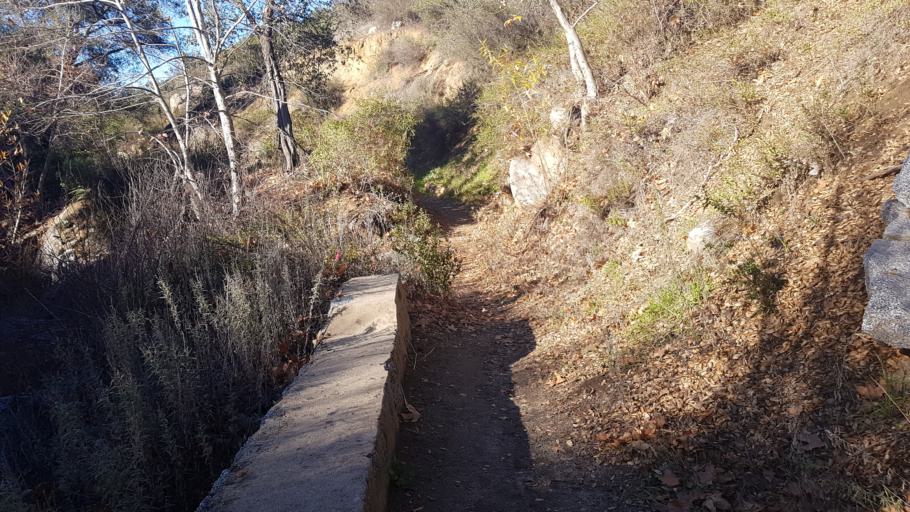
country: US
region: California
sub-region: San Diego County
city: Valley Center
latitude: 33.2212
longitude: -116.9331
